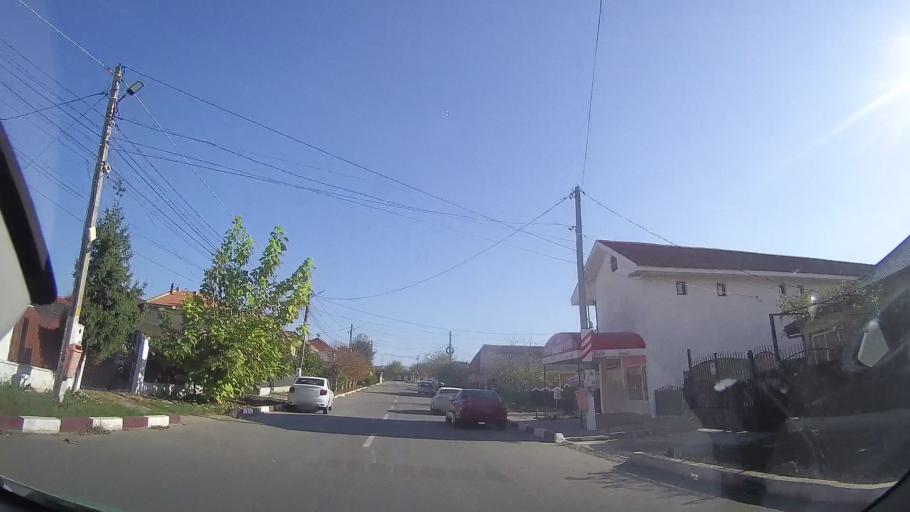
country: RO
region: Constanta
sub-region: Comuna Costinesti
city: Schitu
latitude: 43.9407
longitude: 28.6300
